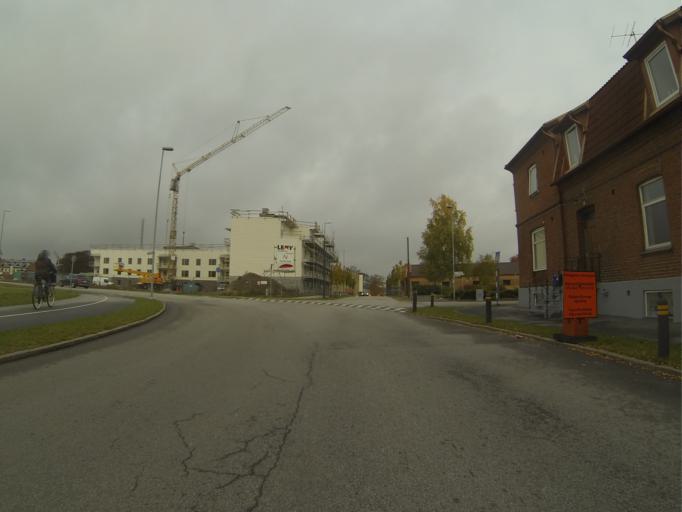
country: SE
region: Skane
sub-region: Sjobo Kommun
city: Sjoebo
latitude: 55.6301
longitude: 13.7050
